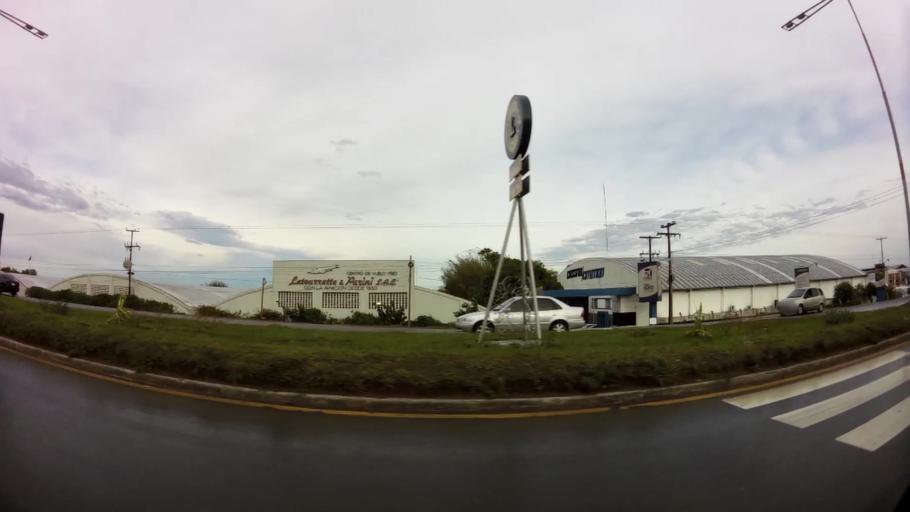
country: PY
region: Central
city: Fernando de la Mora
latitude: -25.2520
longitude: -57.5131
